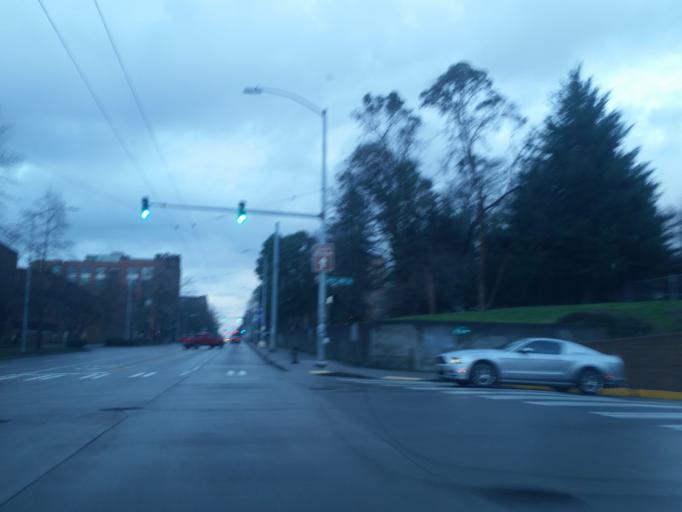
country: US
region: Washington
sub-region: King County
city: Seattle
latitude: 47.6568
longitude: -122.3120
